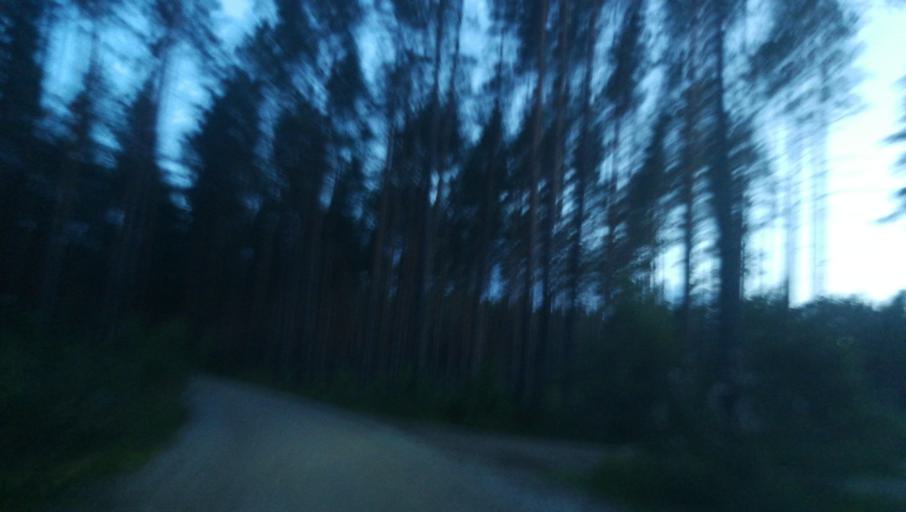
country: LV
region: Valmieras Rajons
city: Valmiera
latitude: 57.5145
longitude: 25.4095
